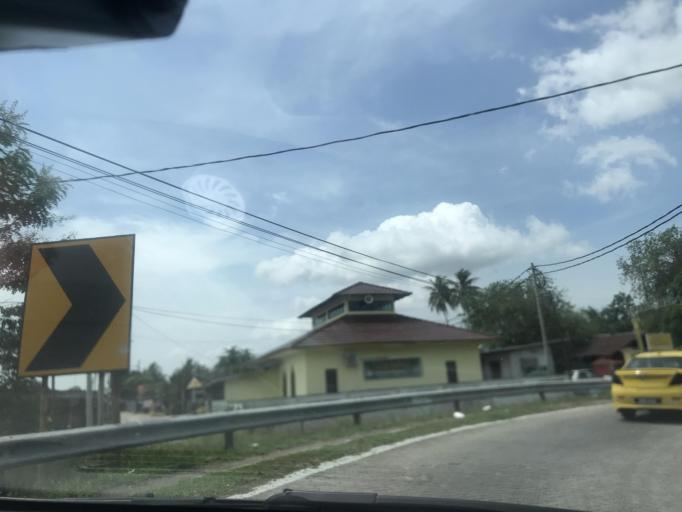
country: MY
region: Kelantan
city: Tumpat
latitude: 6.2050
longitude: 102.1501
